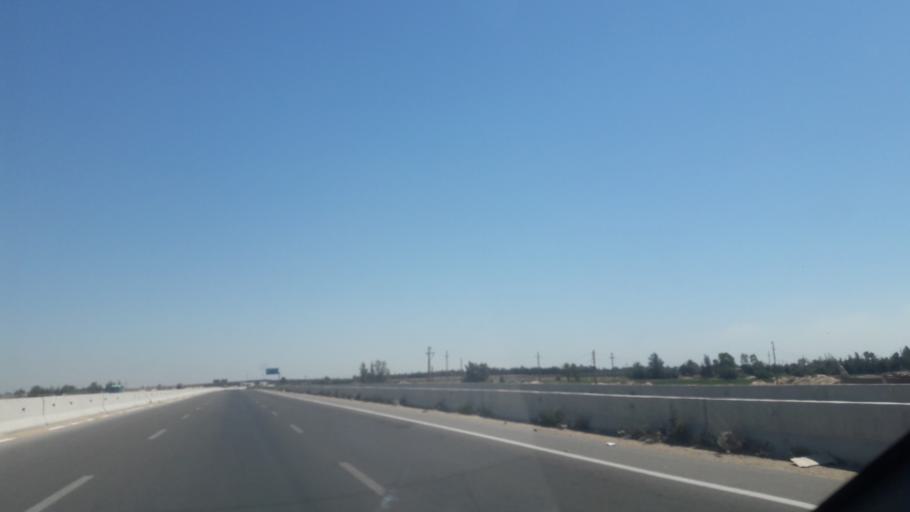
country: EG
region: Al Isma'iliyah
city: Ismailia
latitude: 30.8150
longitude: 32.1665
